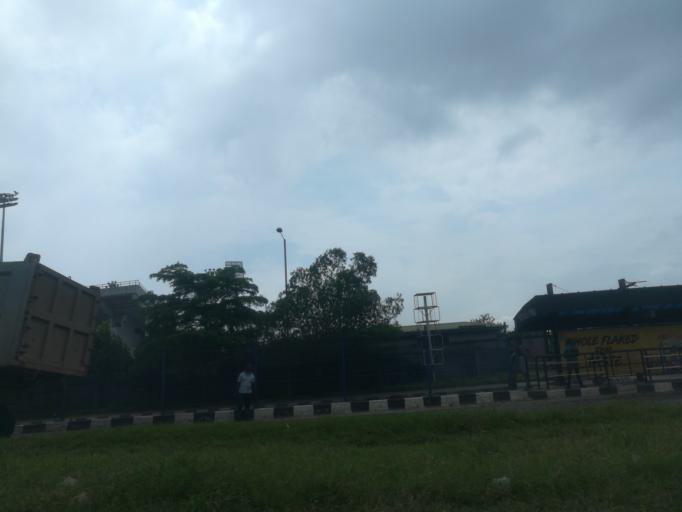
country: NG
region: Lagos
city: Surulere
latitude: 6.4962
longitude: 3.3616
